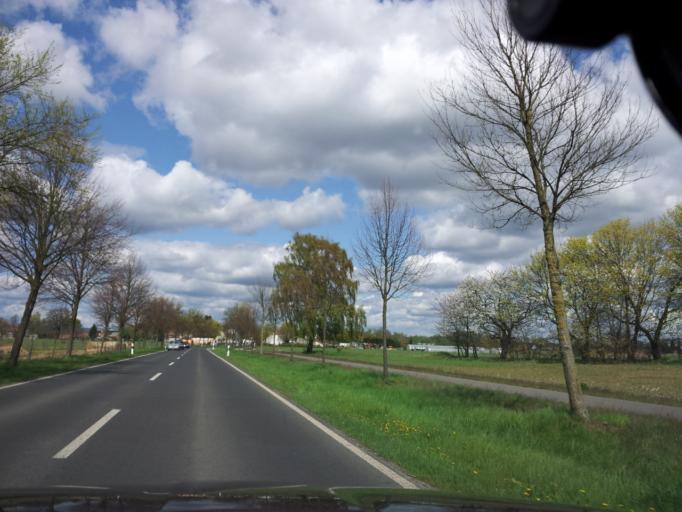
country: DE
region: Brandenburg
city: Rudnitz
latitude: 52.7165
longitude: 13.6209
